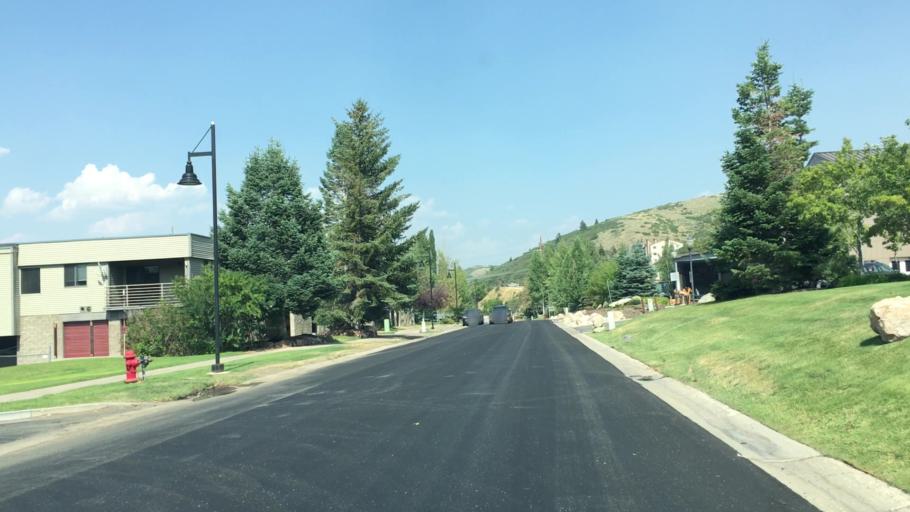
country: US
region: Utah
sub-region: Summit County
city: Park City
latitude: 40.6585
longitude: -111.5051
